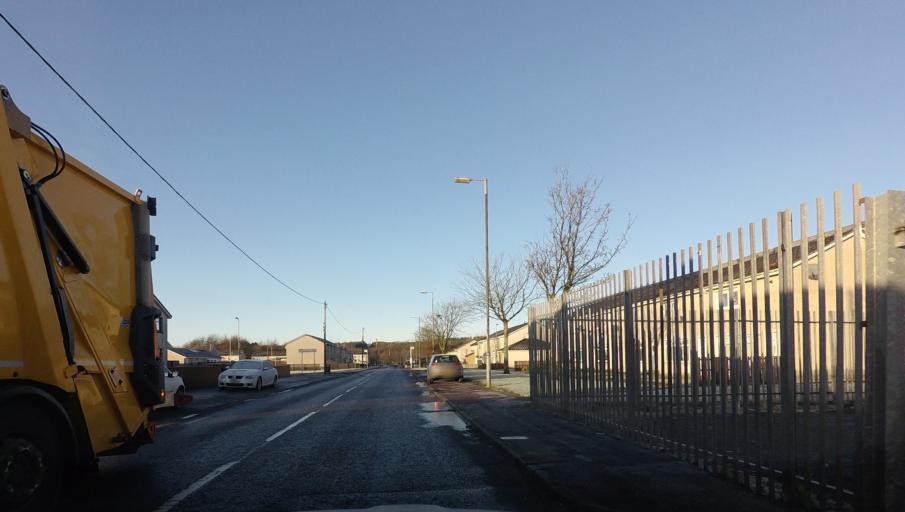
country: GB
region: Scotland
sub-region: North Lanarkshire
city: Shotts
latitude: 55.8237
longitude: -3.8108
